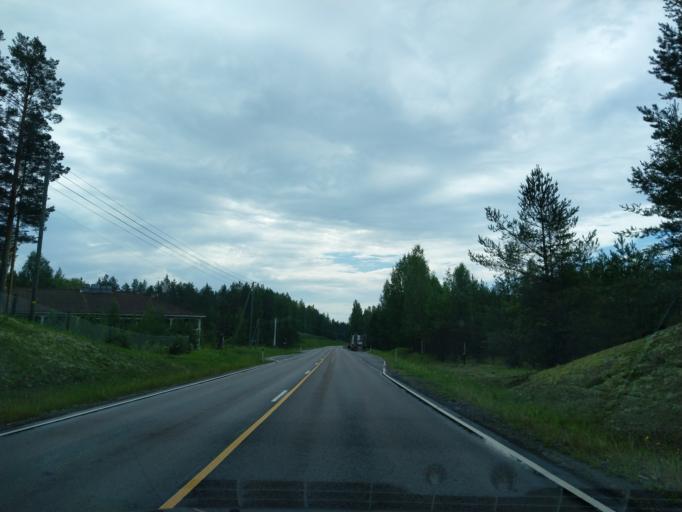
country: FI
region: Southern Savonia
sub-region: Savonlinna
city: Punkaharju
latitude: 61.6874
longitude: 29.4202
